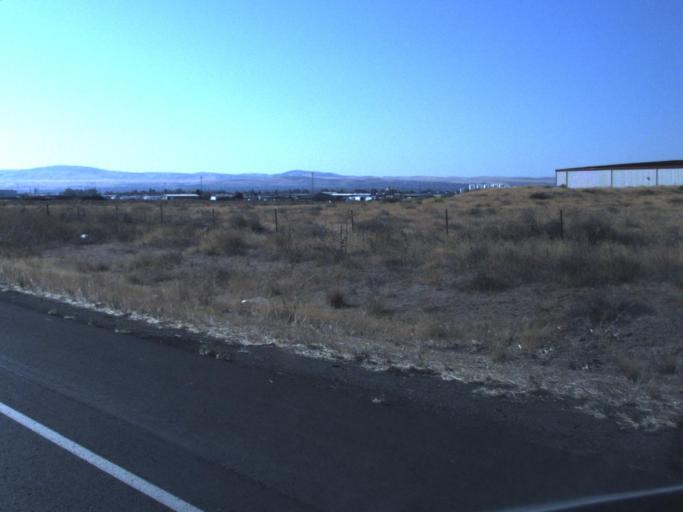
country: US
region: Washington
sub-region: Franklin County
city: Pasco
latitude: 46.2716
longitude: -119.0892
